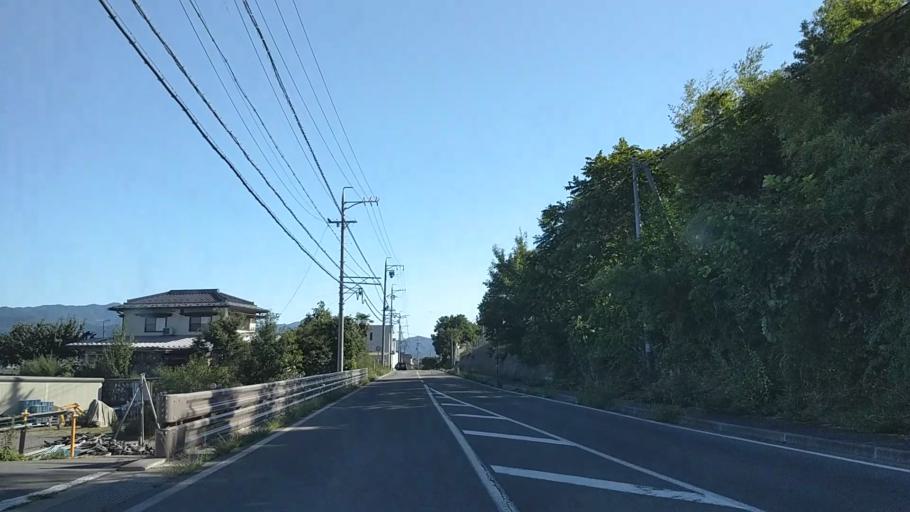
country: JP
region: Nagano
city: Nagano-shi
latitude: 36.5962
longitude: 138.1322
